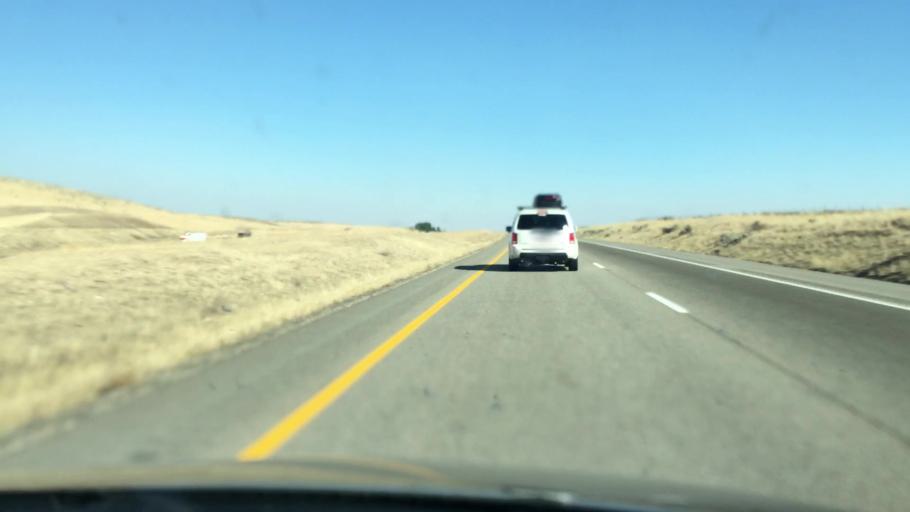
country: US
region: Idaho
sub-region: Ada County
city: Boise
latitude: 43.4857
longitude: -116.1190
